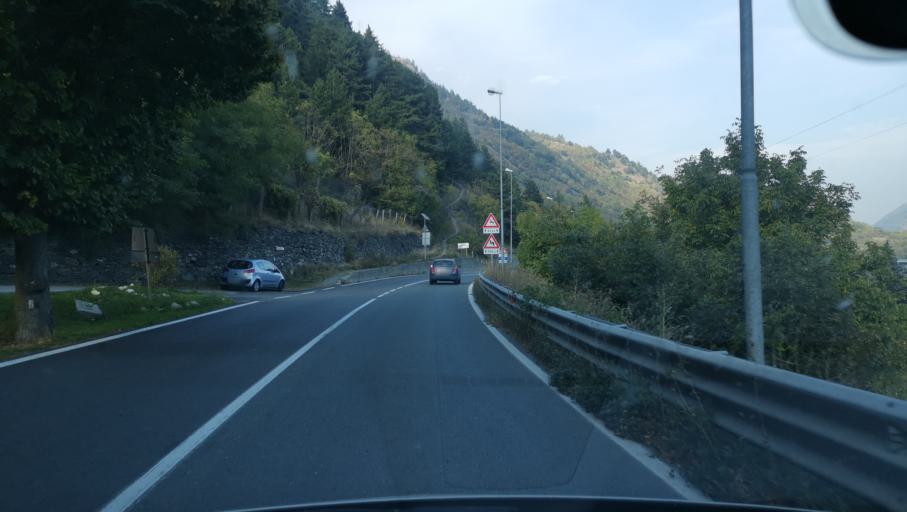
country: IT
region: Piedmont
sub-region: Provincia di Torino
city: Salbertrand
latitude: 45.0737
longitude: 6.8853
